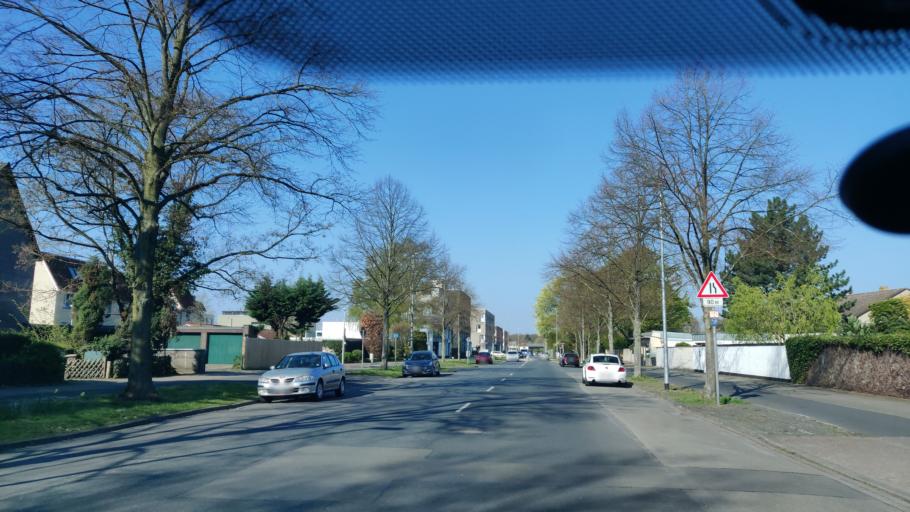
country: DE
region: Lower Saxony
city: Laatzen
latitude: 52.3599
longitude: 9.8072
